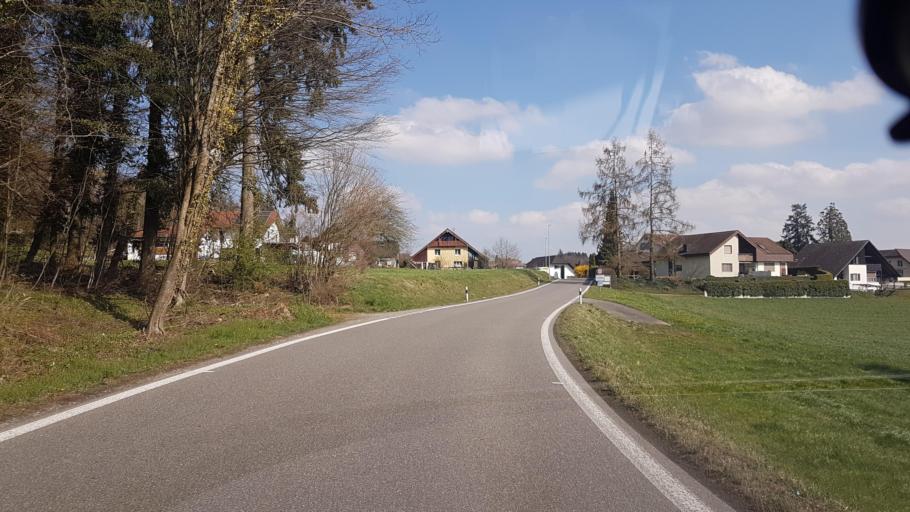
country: CH
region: Aargau
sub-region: Bezirk Bremgarten
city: Bremgarten
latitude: 47.3158
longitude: 8.3375
